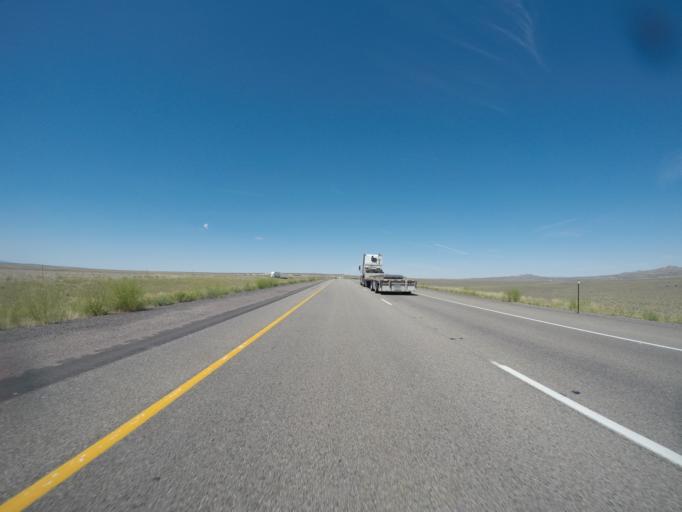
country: US
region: Wyoming
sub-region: Carbon County
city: Saratoga
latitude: 41.7421
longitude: -106.8040
